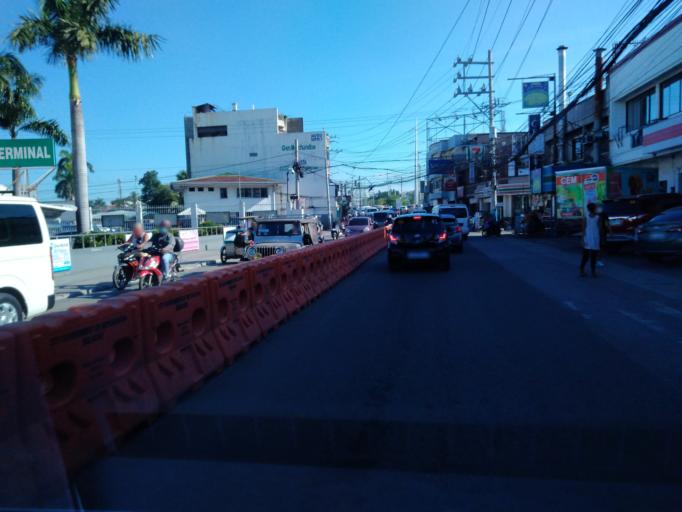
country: PH
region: Central Luzon
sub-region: Province of Bulacan
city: Meycauayan
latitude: 14.7439
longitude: 120.9711
